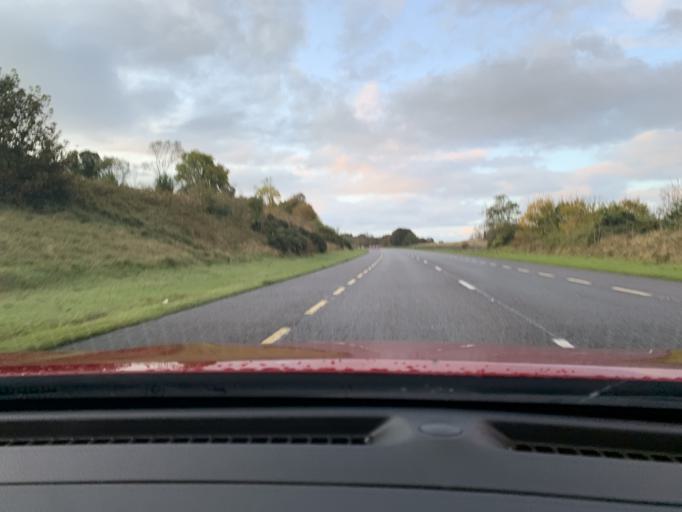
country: IE
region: Connaught
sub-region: Roscommon
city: Boyle
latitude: 54.0514
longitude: -8.3404
